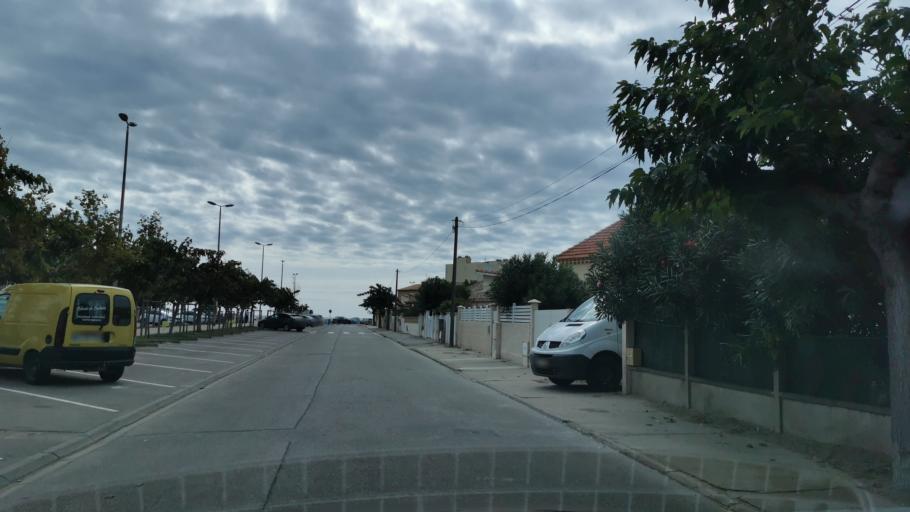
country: FR
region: Languedoc-Roussillon
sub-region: Departement de l'Aude
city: Armissan
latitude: 43.1611
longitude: 3.1678
